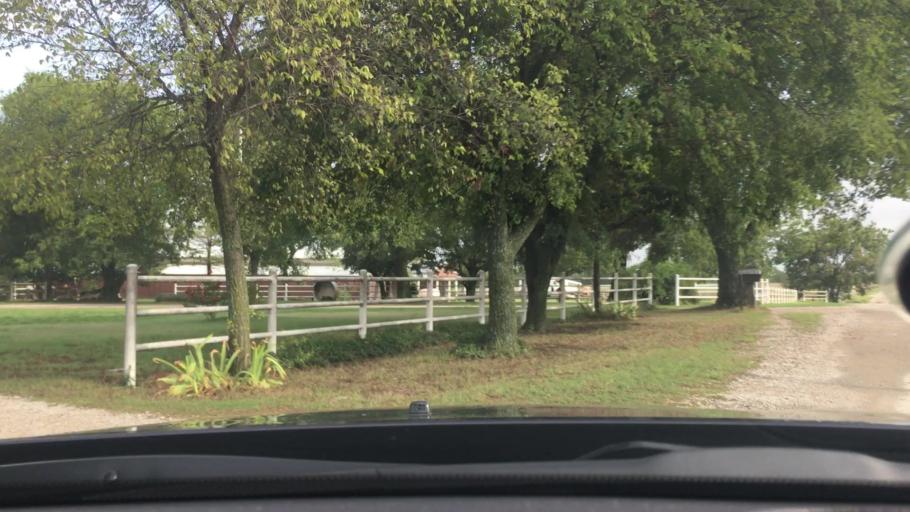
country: US
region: Oklahoma
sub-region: Carter County
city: Lone Grove
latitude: 34.2173
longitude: -97.2650
